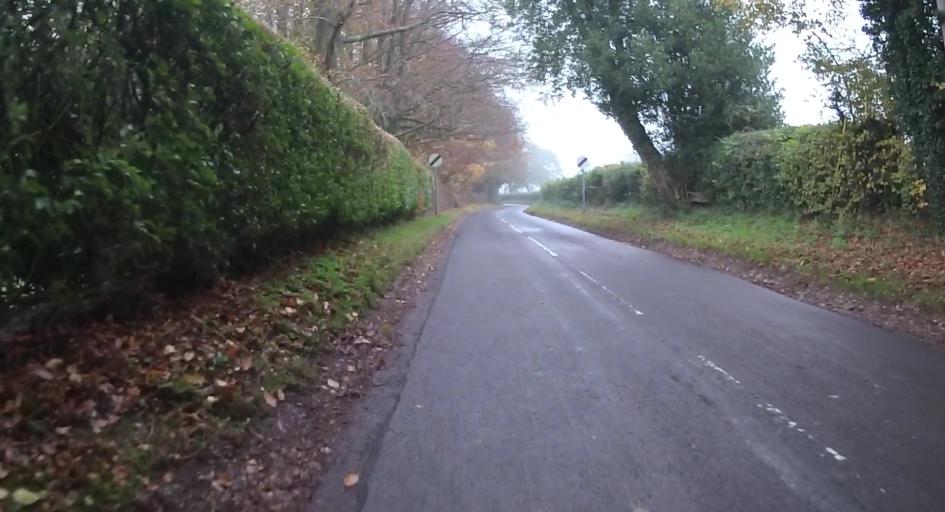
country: GB
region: England
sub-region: Hampshire
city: Alton
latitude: 51.1842
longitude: -0.9815
